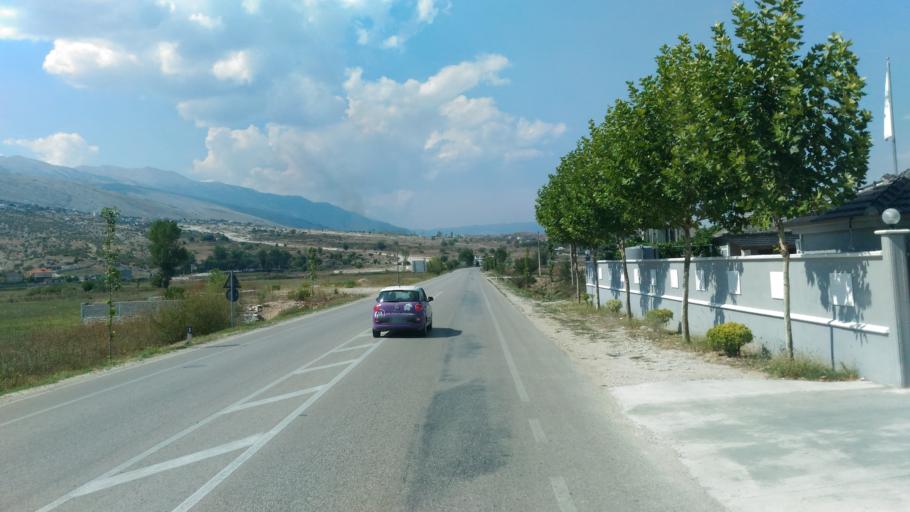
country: AL
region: Gjirokaster
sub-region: Rrethi i Gjirokastres
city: Dervician
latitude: 40.0358
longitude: 20.1801
